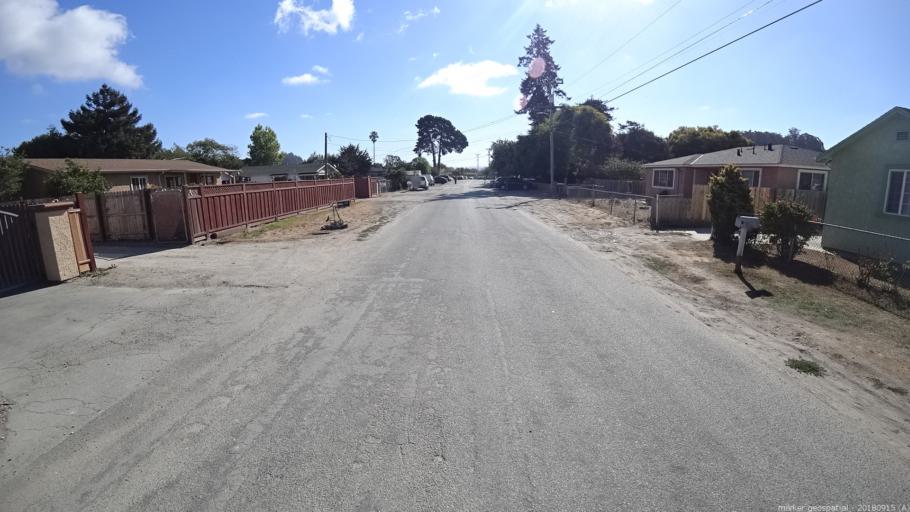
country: US
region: California
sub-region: Monterey County
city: Las Lomas
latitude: 36.8631
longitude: -121.7345
